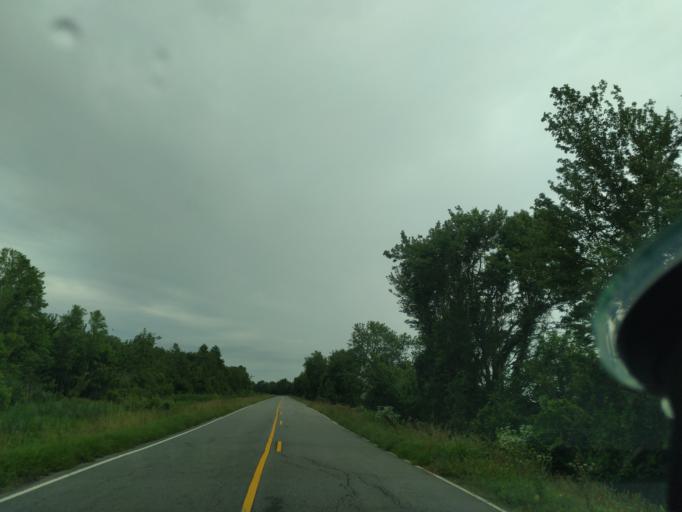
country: US
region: North Carolina
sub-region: Washington County
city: Plymouth
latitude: 35.7798
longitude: -76.5243
